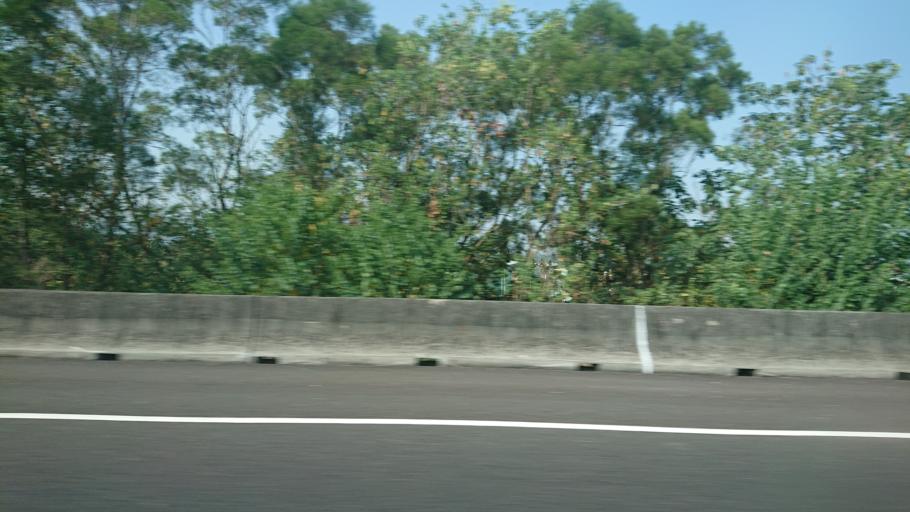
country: TW
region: Taiwan
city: Lugu
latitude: 23.8265
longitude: 120.7079
